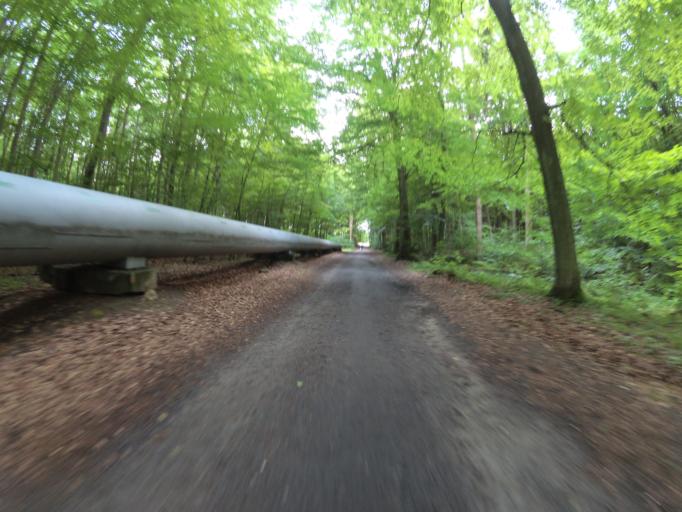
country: PL
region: Pomeranian Voivodeship
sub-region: Gdynia
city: Wielki Kack
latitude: 54.5015
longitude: 18.4938
